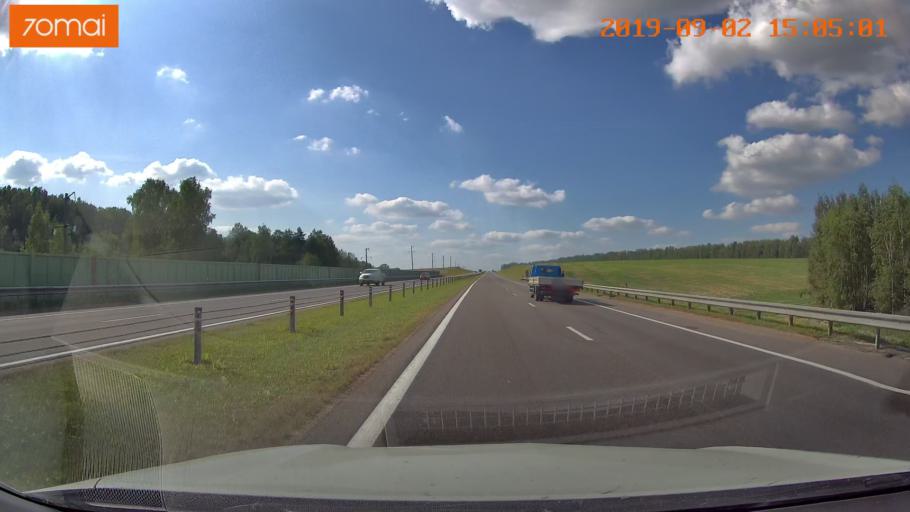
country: BY
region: Mogilev
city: Vishow
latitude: 53.9785
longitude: 29.9411
